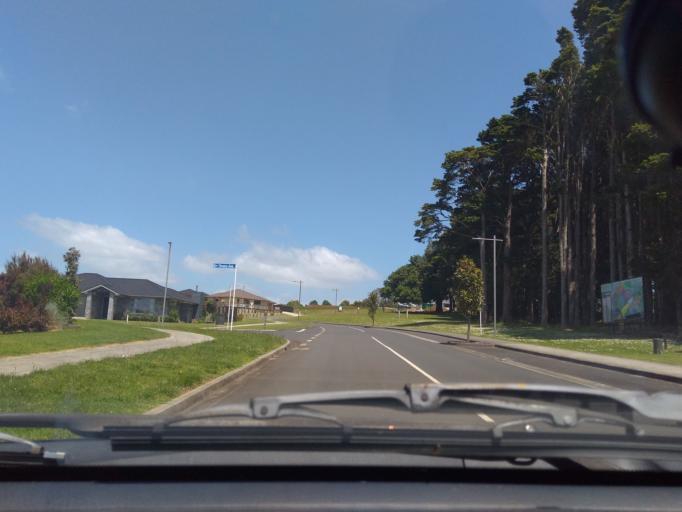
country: NZ
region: Northland
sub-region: Whangarei
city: Whangarei
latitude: -35.6751
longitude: 174.3165
